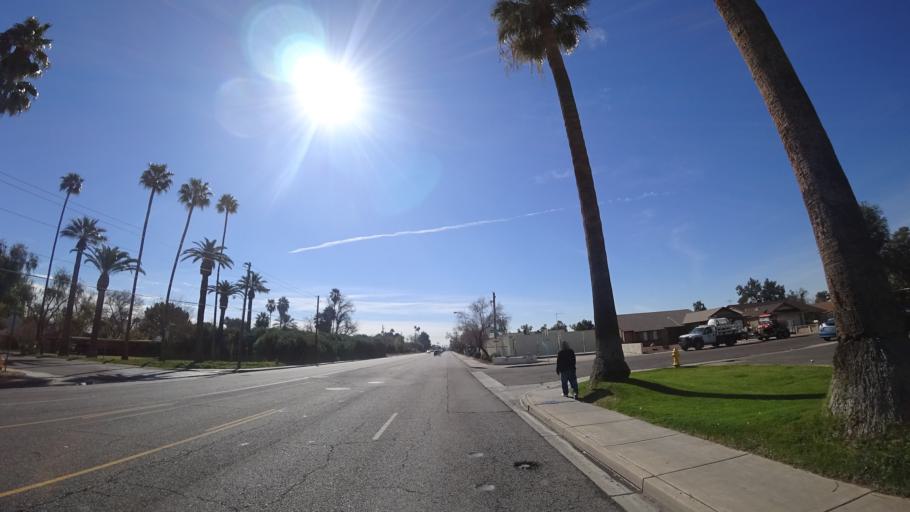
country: US
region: Arizona
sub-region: Maricopa County
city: Glendale
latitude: 33.5570
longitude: -112.1863
